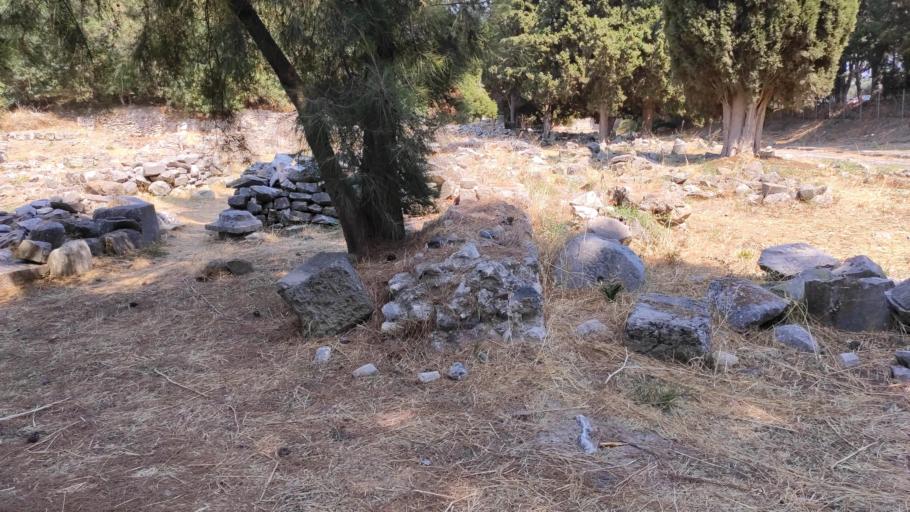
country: GR
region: South Aegean
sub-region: Nomos Dodekanisou
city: Kos
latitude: 36.8905
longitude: 27.2845
